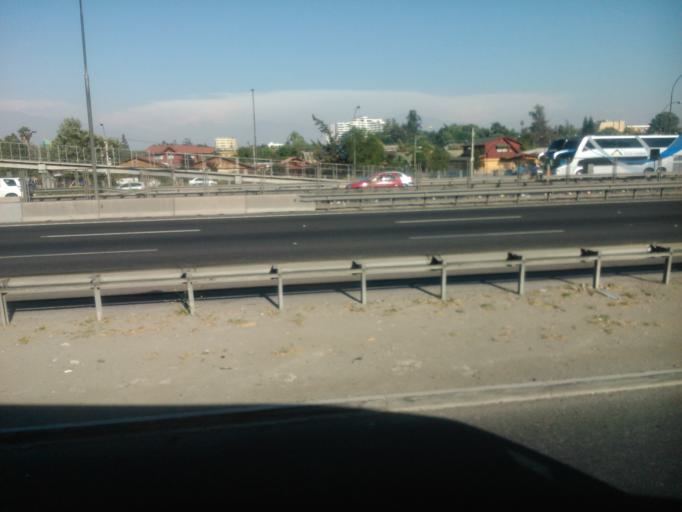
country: CL
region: Santiago Metropolitan
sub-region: Provincia de Maipo
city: San Bernardo
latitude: -33.5898
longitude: -70.7151
